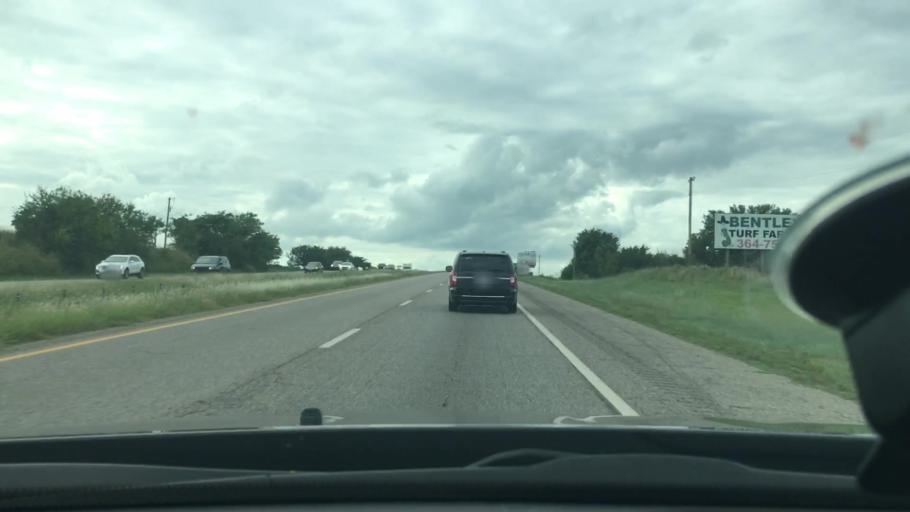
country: US
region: Oklahoma
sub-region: Cleveland County
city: Noble
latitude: 35.1047
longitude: -97.4318
